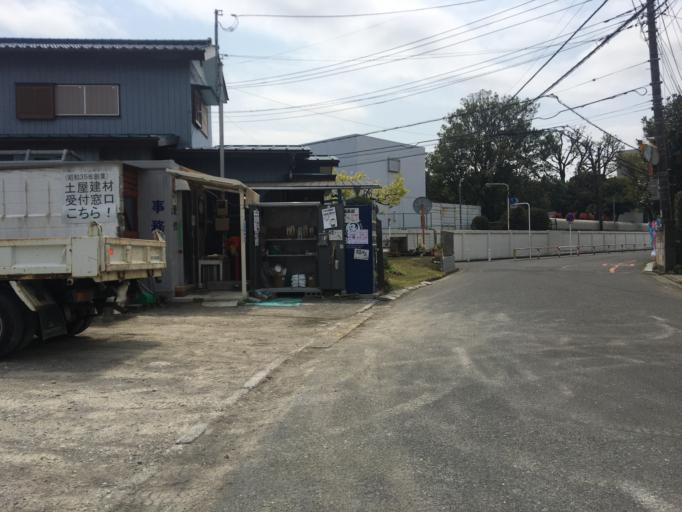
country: JP
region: Saitama
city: Kamifukuoka
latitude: 35.8841
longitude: 139.5222
